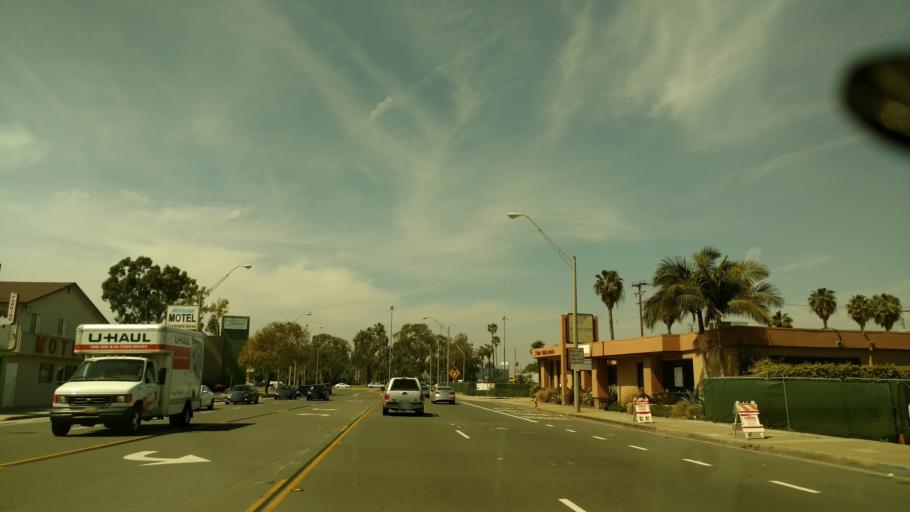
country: US
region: California
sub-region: Los Angeles County
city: Signal Hill
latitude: 33.7884
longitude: -118.1402
